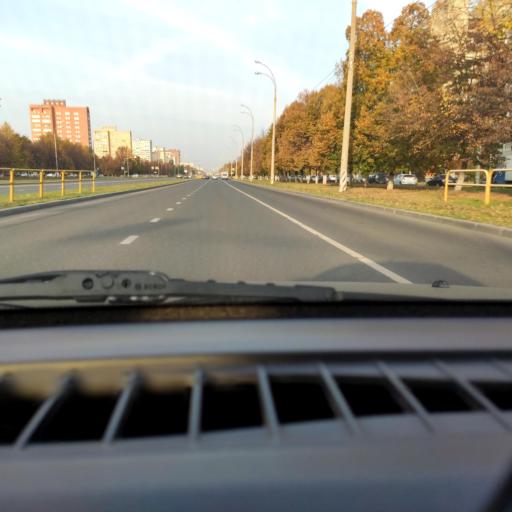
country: RU
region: Samara
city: Tol'yatti
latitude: 53.5257
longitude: 49.3212
